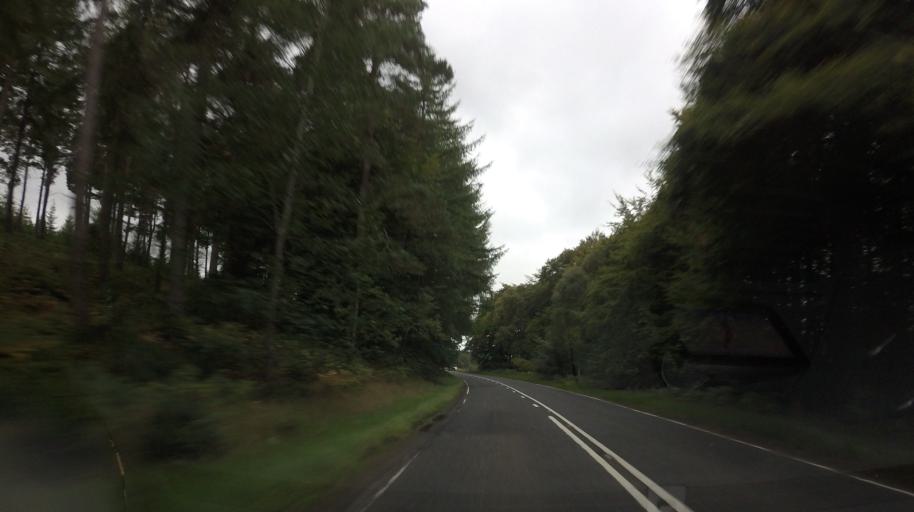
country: GB
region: Scotland
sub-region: Aberdeenshire
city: Torphins
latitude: 57.1978
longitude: -2.5830
